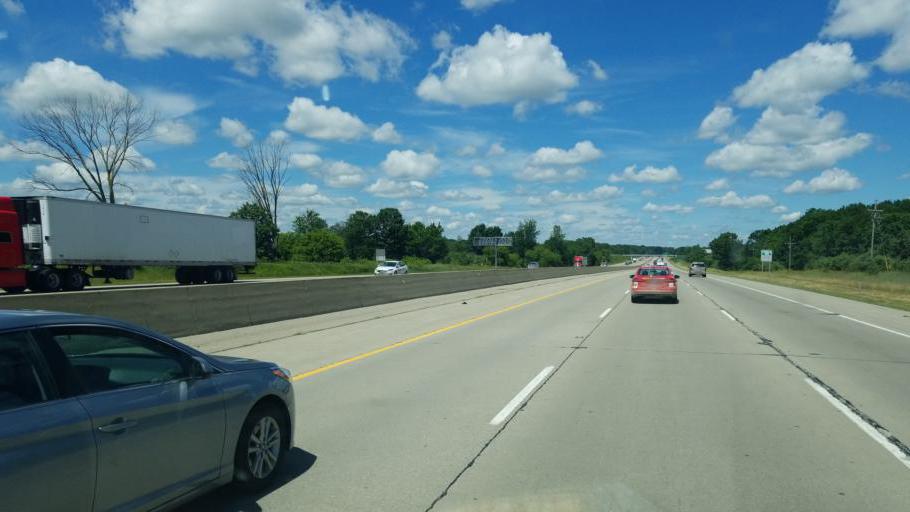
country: US
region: Michigan
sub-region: Livingston County
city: Brighton
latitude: 42.5588
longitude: -83.8248
